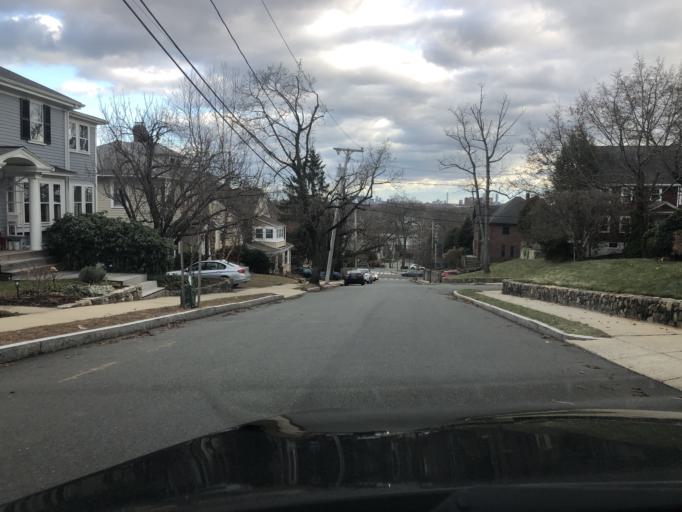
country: US
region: Massachusetts
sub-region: Middlesex County
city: Arlington
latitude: 42.4097
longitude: -71.1605
